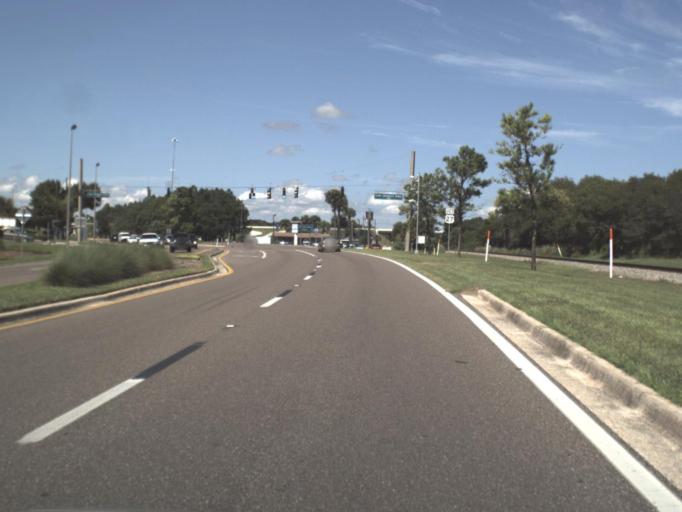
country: US
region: Florida
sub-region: Polk County
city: Haines City
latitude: 28.1062
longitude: -81.6368
